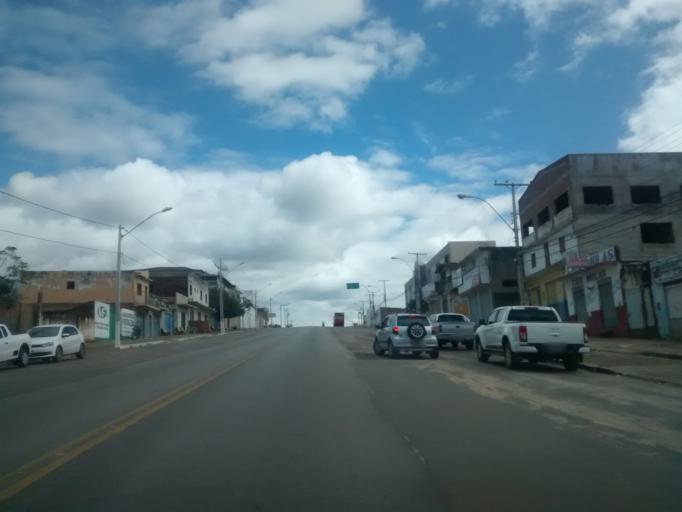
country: BR
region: Bahia
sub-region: Brumado
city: Brumado
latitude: -14.2159
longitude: -41.6814
